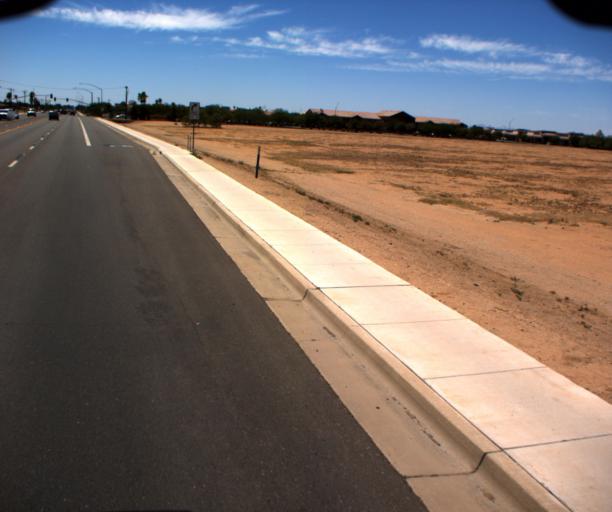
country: US
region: Arizona
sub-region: Pinal County
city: Casa Grande
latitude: 32.8797
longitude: -111.7028
